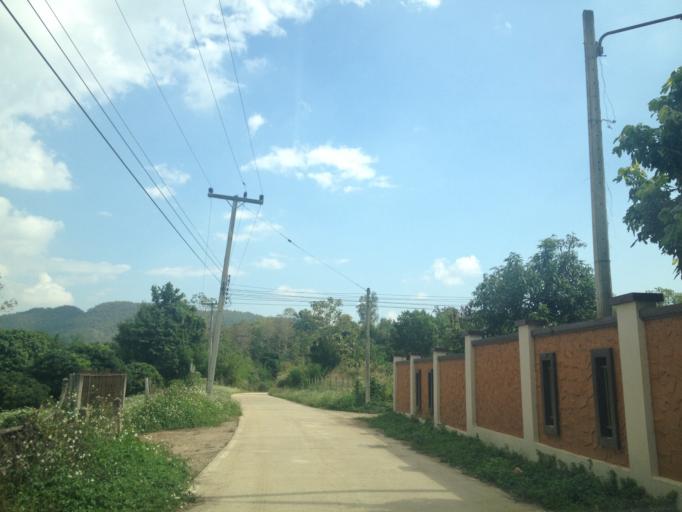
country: TH
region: Chiang Mai
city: Hang Dong
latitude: 18.7259
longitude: 98.8772
